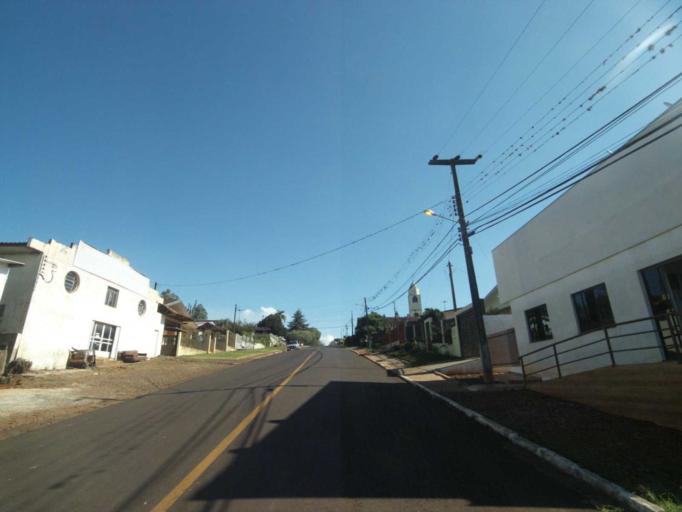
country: BR
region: Parana
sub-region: Laranjeiras Do Sul
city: Laranjeiras do Sul
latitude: -25.3804
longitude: -52.2012
